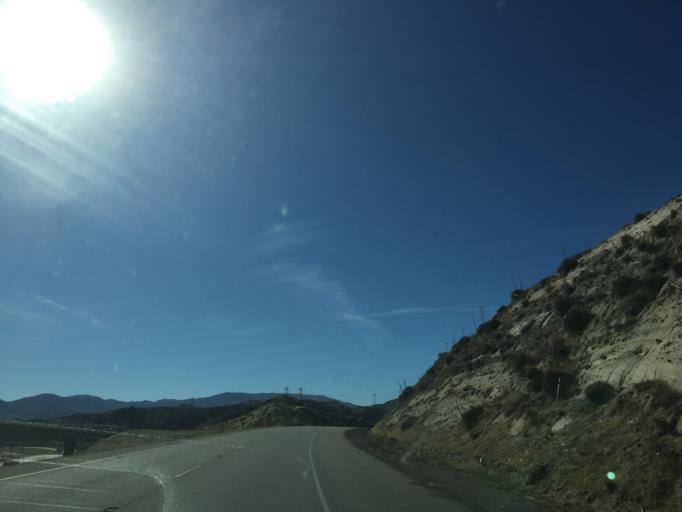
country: US
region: California
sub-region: Kern County
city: Lebec
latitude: 34.7669
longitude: -118.7876
